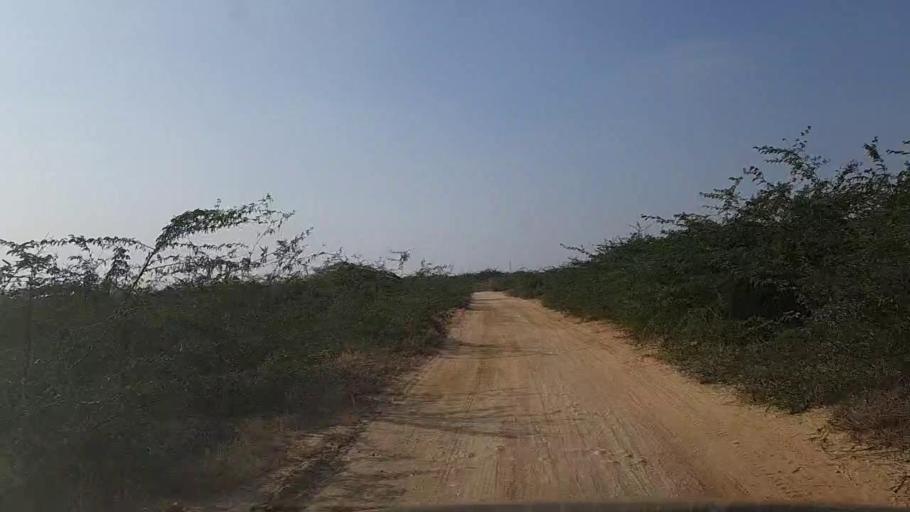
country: PK
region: Sindh
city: Gharo
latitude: 24.7513
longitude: 67.5537
